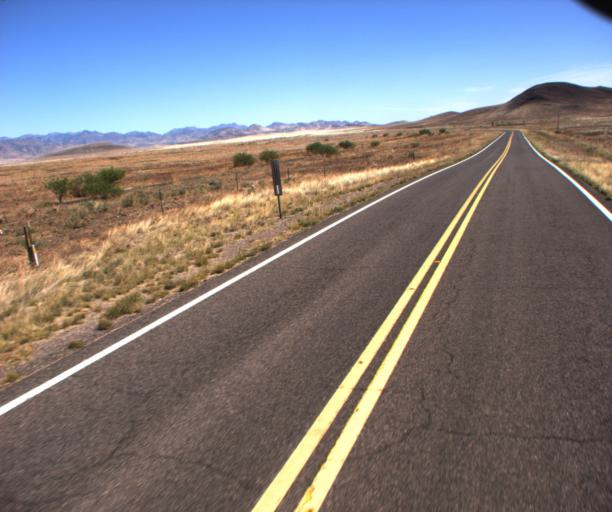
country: US
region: Arizona
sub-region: Cochise County
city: Douglas
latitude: 31.5533
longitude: -109.2689
